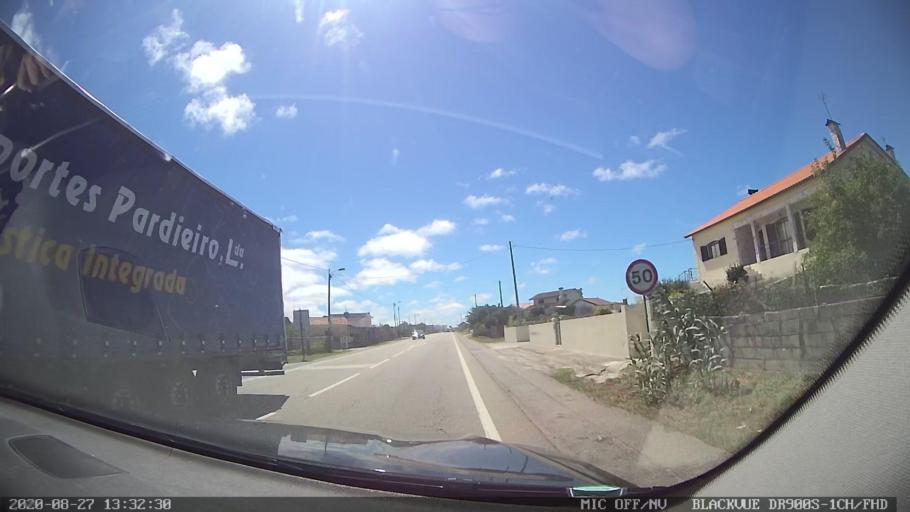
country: PT
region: Aveiro
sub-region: Vagos
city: Vagos
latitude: 40.4875
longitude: -8.6877
